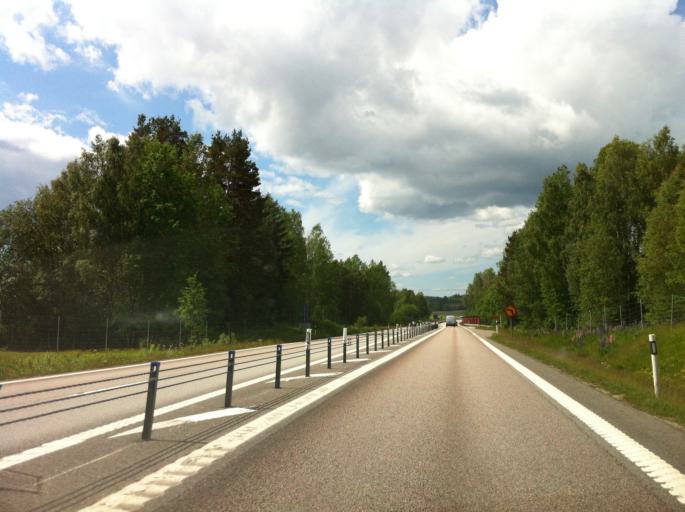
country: SE
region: Vaermland
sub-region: Saffle Kommun
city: Saeffle
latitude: 59.1223
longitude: 12.8583
